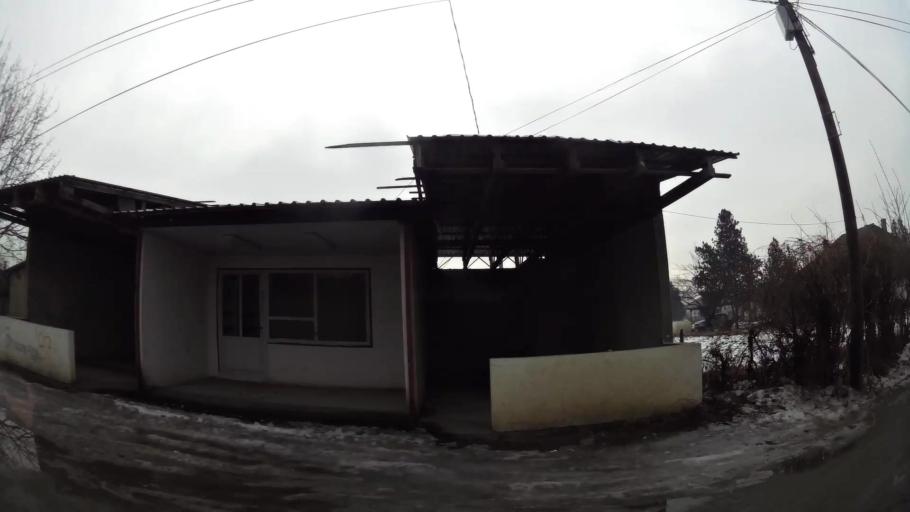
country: MK
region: Ilinden
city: Ilinden
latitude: 41.9943
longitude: 21.5783
